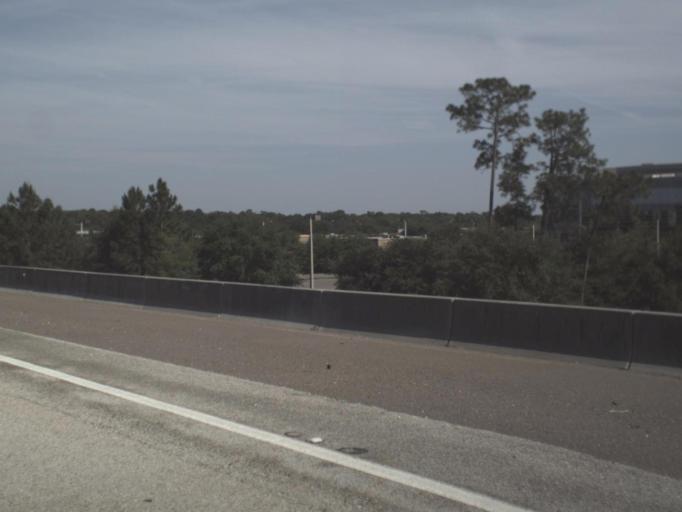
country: US
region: Florida
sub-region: Duval County
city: Jacksonville
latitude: 30.2513
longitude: -81.5836
